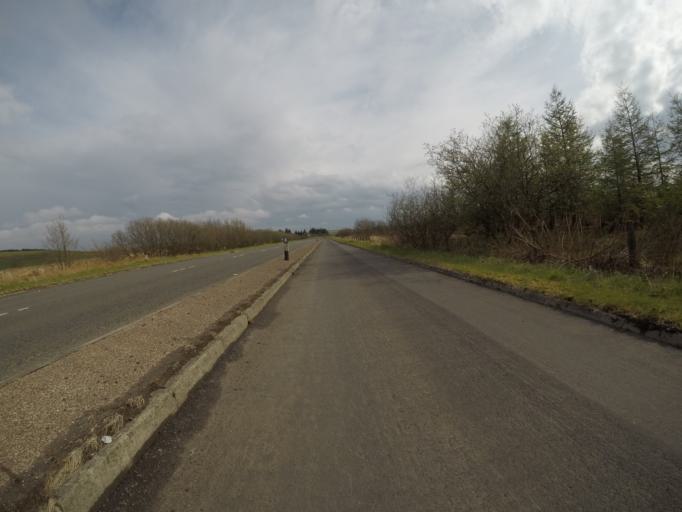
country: GB
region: Scotland
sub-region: East Renfrewshire
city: Neilston
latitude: 55.6994
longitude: -4.3948
